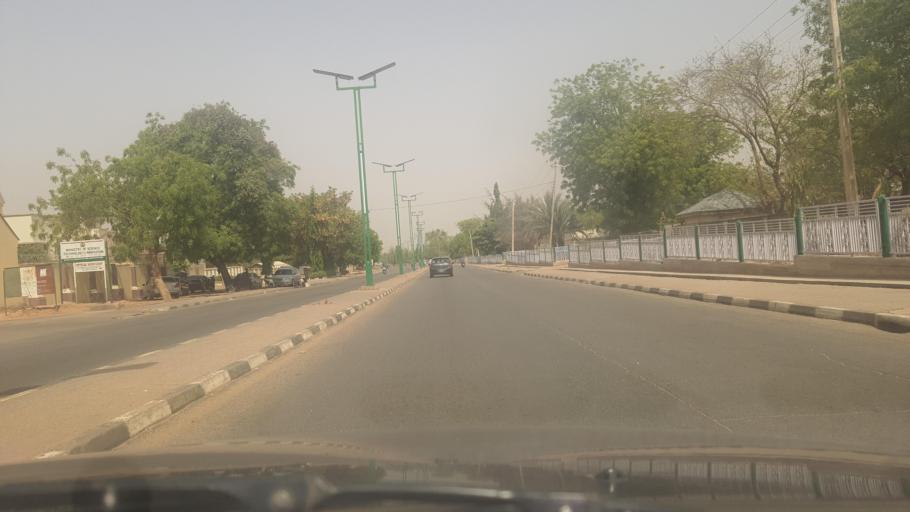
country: NG
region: Gombe
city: Gombe
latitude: 10.2826
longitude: 11.1550
